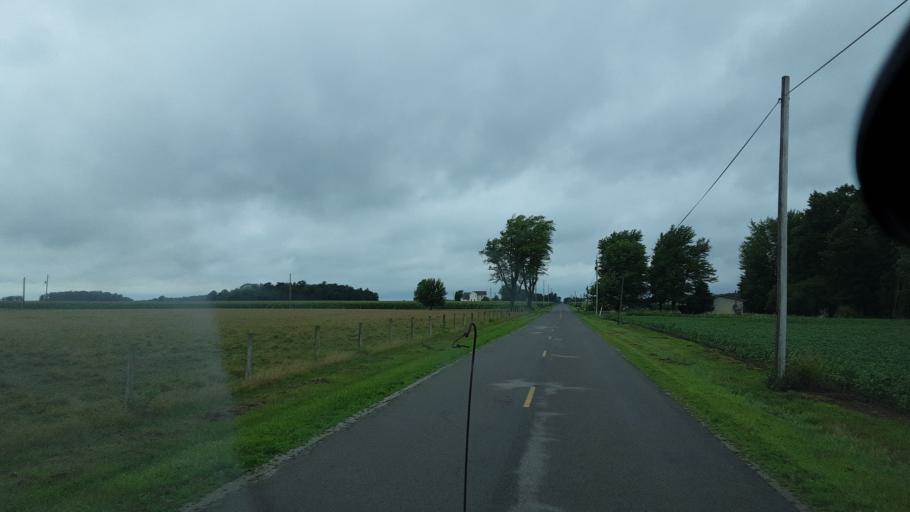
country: US
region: Ohio
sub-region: Van Wert County
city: Convoy
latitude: 40.8276
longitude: -84.7460
